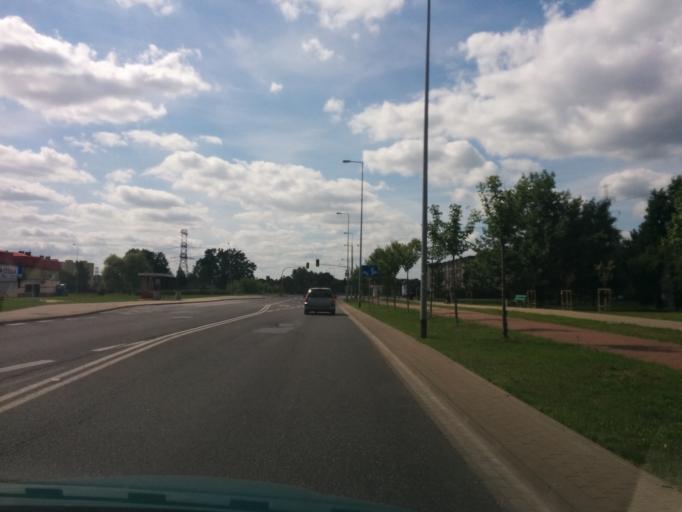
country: PL
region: Masovian Voivodeship
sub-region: Warszawa
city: Bialoleka
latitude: 52.3285
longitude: 20.9408
